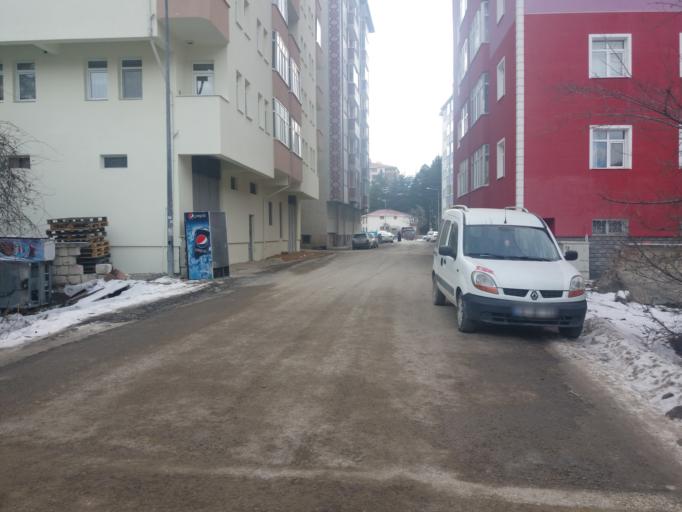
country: TR
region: Gumushane
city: Gumushkhane
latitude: 40.4523
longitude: 39.4930
